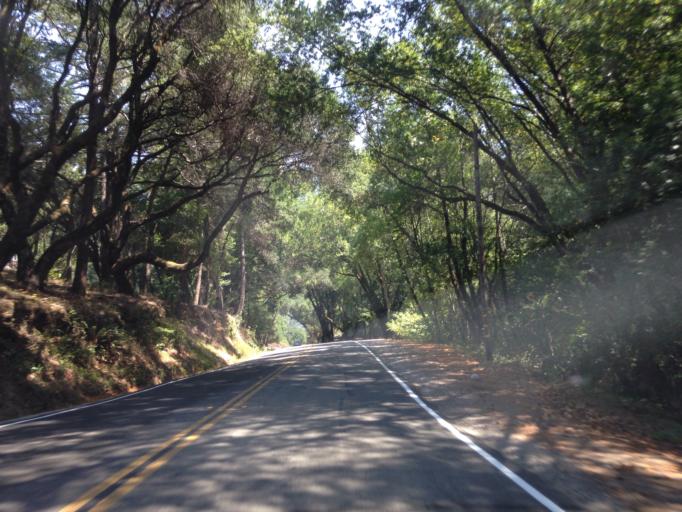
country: US
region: California
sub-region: Marin County
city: Lagunitas-Forest Knolls
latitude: 38.0519
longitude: -122.6709
